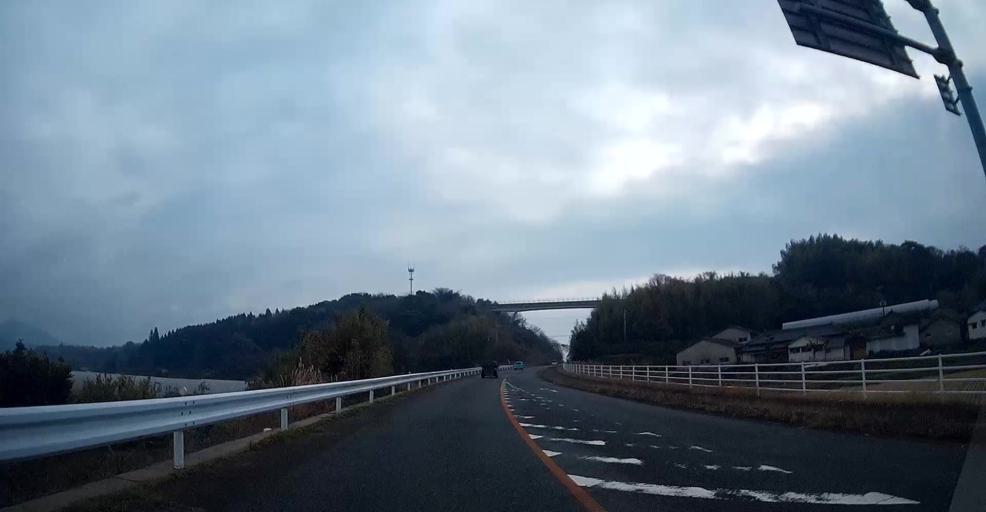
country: JP
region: Kumamoto
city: Matsubase
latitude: 32.6269
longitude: 130.5324
